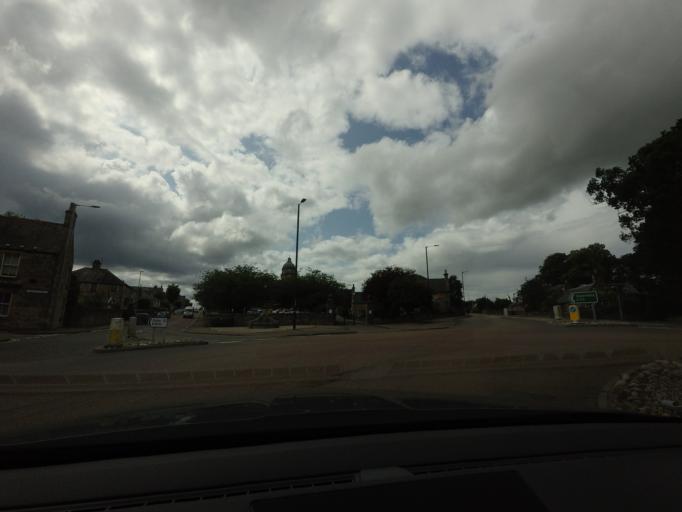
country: GB
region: Scotland
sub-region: Moray
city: Elgin
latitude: 57.6463
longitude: -3.3260
